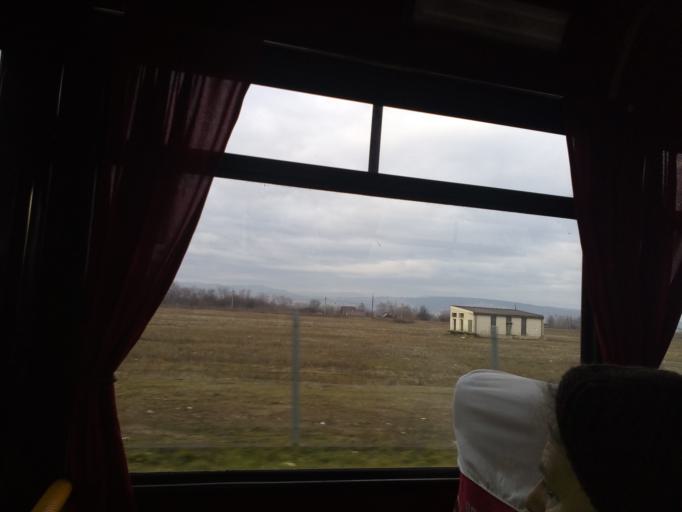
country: PL
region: Lesser Poland Voivodeship
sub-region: Powiat nowosadecki
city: Nowy Sacz
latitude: 49.5967
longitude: 20.6829
